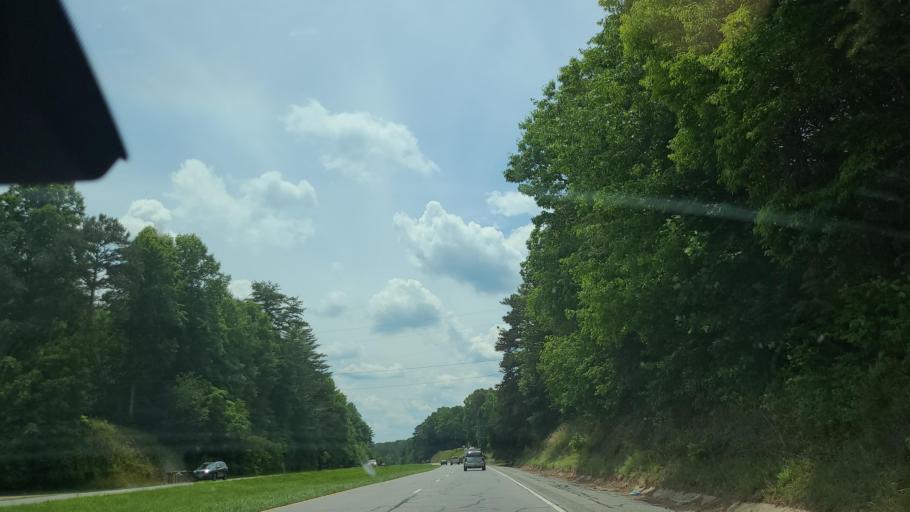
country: US
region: North Carolina
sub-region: Cherokee County
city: Murphy
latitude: 35.0271
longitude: -84.1647
